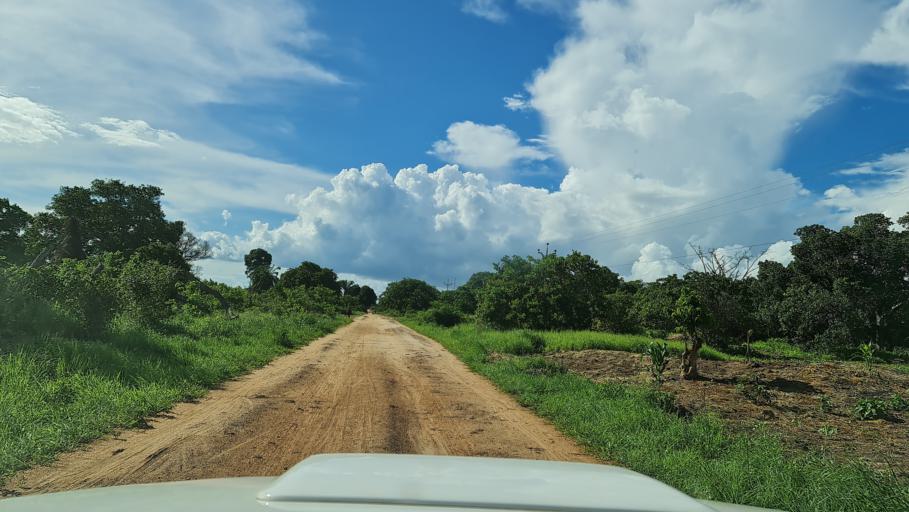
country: MZ
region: Nampula
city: Ilha de Mocambique
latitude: -15.2951
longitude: 40.1216
